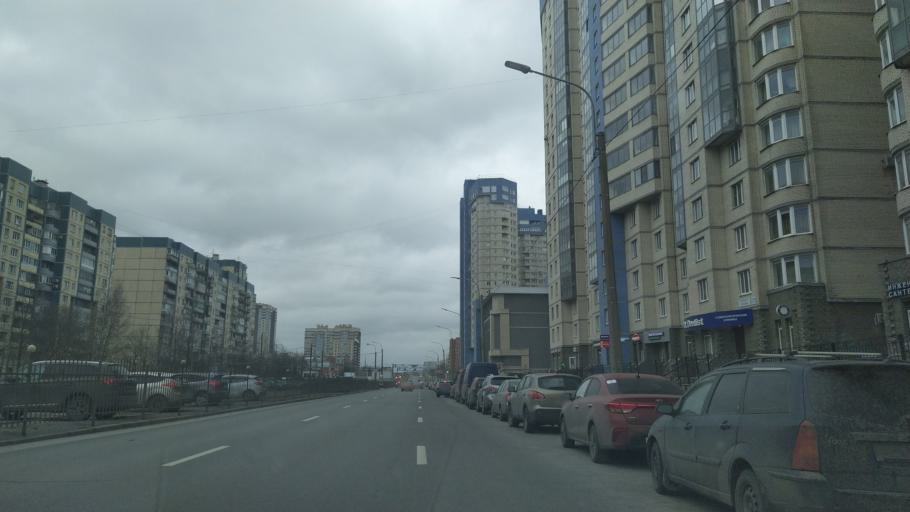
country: RU
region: St.-Petersburg
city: Komendantsky aerodrom
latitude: 60.0143
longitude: 30.2775
